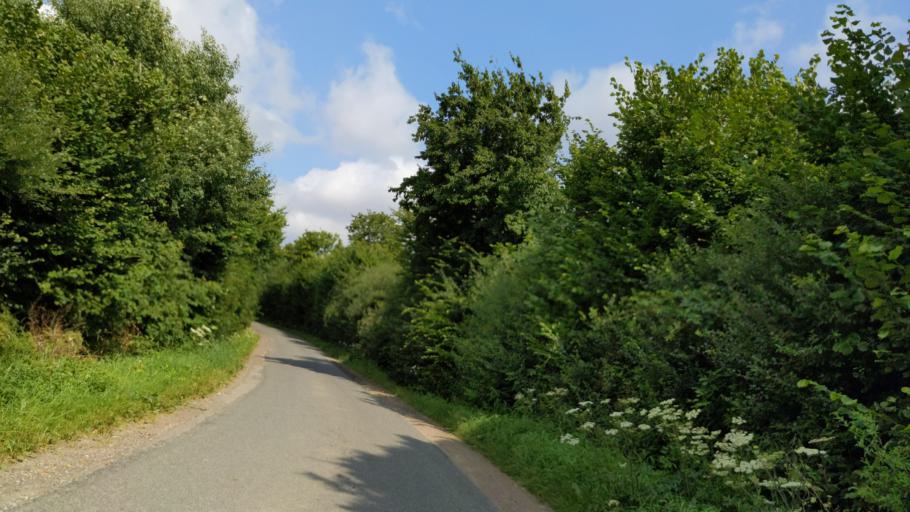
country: DE
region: Schleswig-Holstein
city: Badendorf
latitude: 53.8991
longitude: 10.5995
